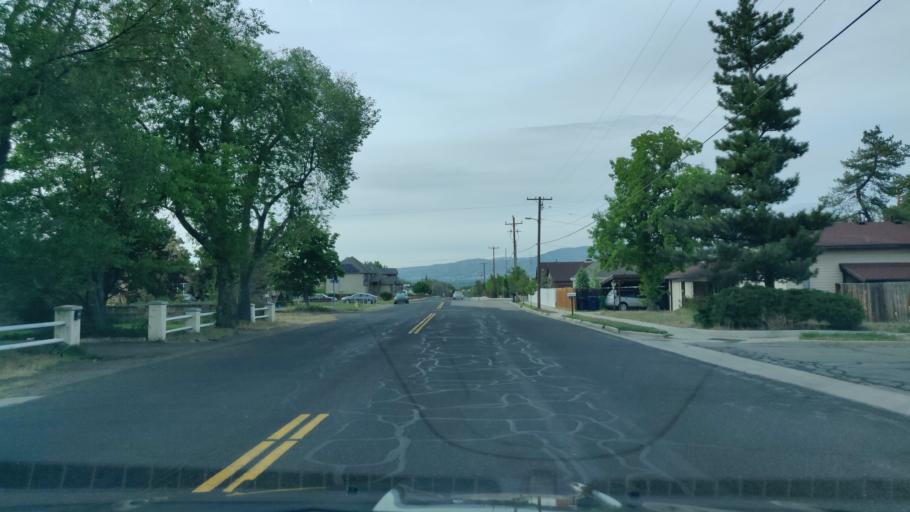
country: US
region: Utah
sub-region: Salt Lake County
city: Little Cottonwood Creek Valley
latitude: 40.6221
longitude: -111.8439
